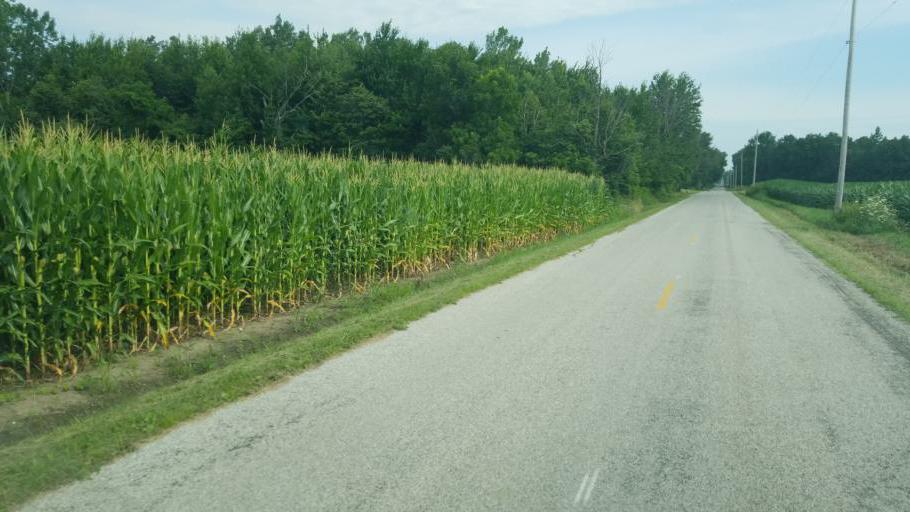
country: US
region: Ohio
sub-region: Marion County
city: Marion
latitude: 40.6323
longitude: -83.3050
